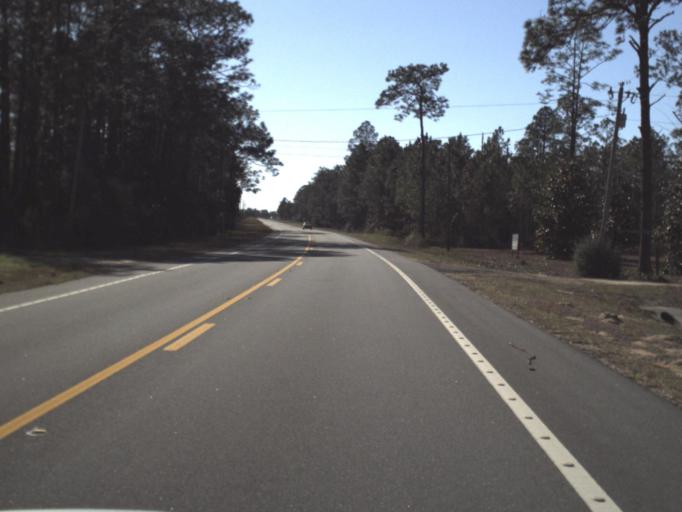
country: US
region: Florida
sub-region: Bay County
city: Youngstown
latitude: 30.4371
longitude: -85.3463
